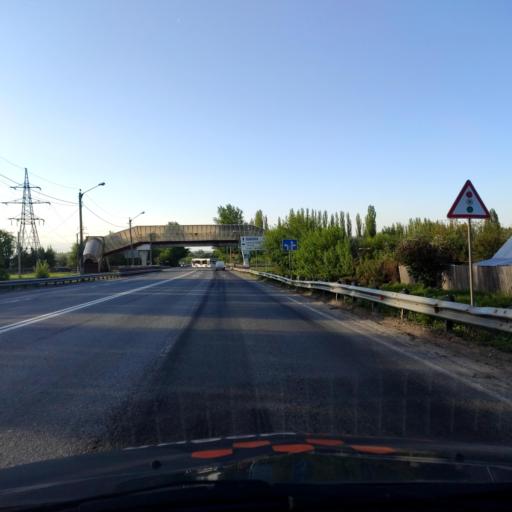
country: RU
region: Lipetsk
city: Yelets
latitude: 52.6009
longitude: 38.4721
